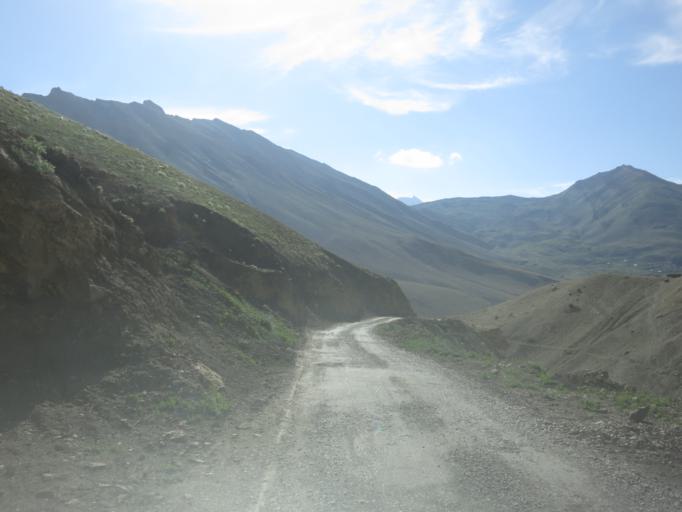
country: IN
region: Himachal Pradesh
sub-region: Kulu
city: Manali
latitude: 32.3246
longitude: 78.0087
